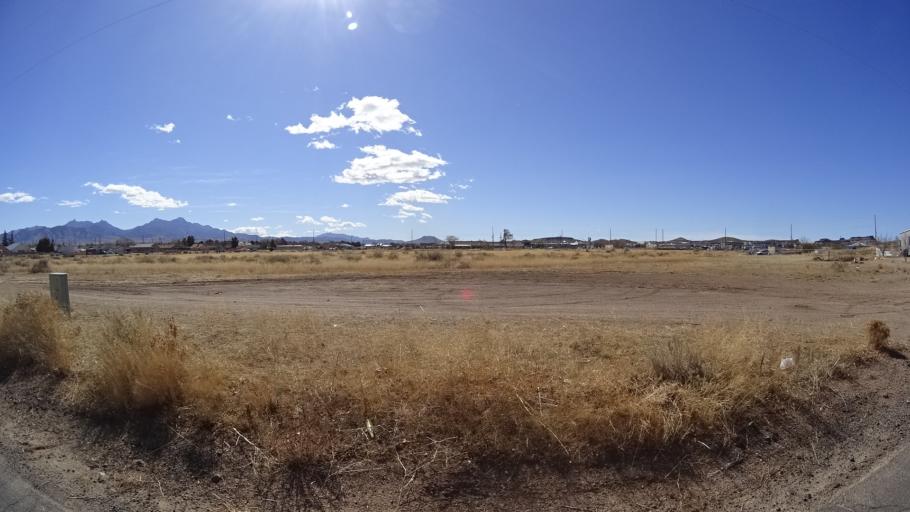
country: US
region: Arizona
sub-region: Mohave County
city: New Kingman-Butler
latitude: 35.2285
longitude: -114.0316
